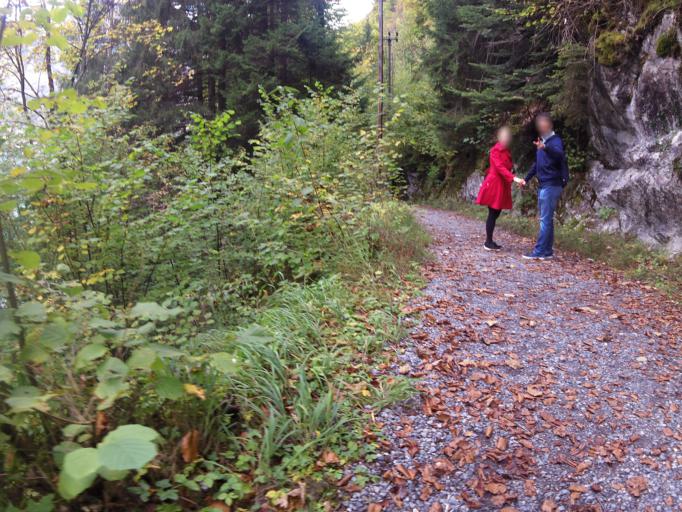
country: CH
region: Bern
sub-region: Interlaken-Oberhasli District
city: Brienz
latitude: 46.7356
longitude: 8.0213
